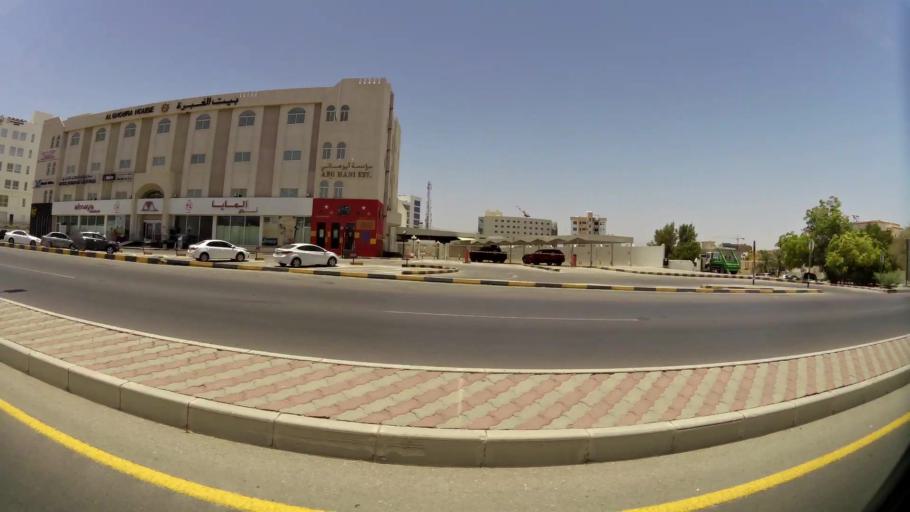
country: OM
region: Muhafazat Masqat
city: Bawshar
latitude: 23.5965
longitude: 58.4096
